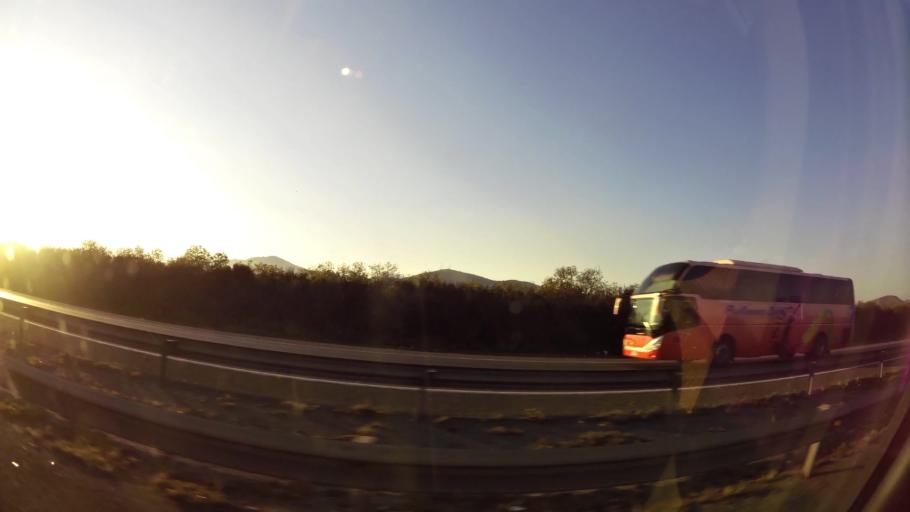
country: CL
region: Santiago Metropolitan
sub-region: Provincia de Talagante
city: Penaflor
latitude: -33.5621
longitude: -70.8376
